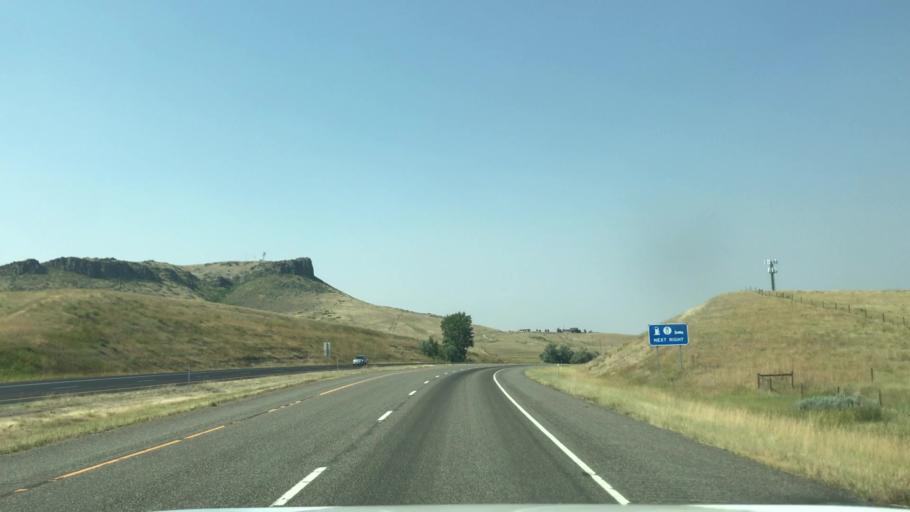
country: US
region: Montana
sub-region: Cascade County
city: Sun Prairie
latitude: 47.2709
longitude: -111.7080
